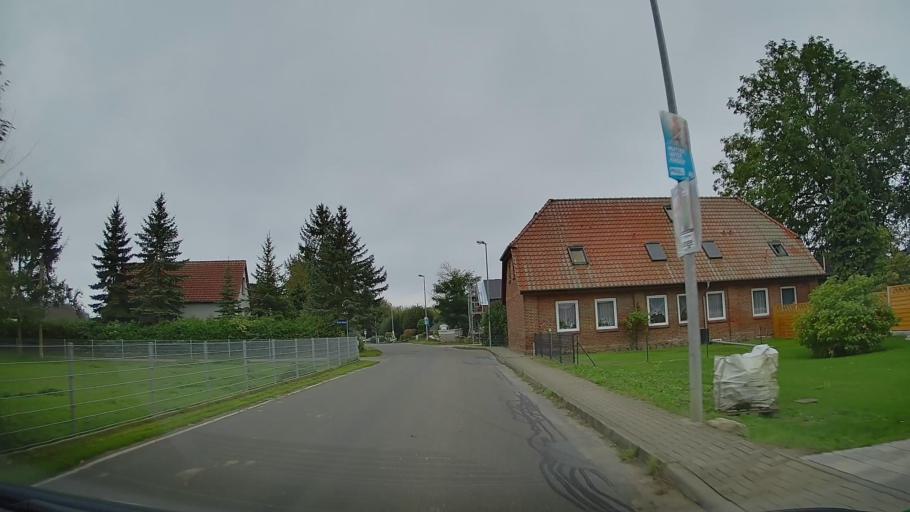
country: DE
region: Mecklenburg-Vorpommern
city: Guestrow
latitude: 53.8108
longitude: 12.1142
